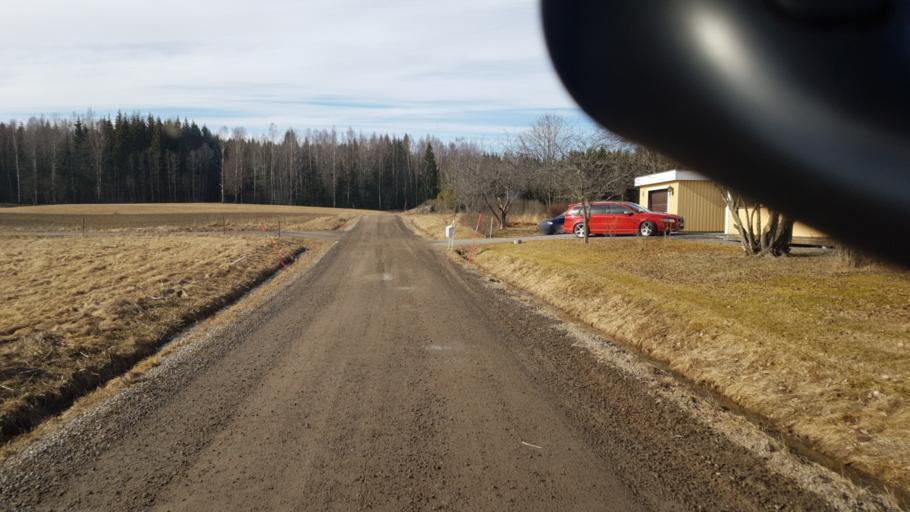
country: SE
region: Vaermland
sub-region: Eda Kommun
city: Amotfors
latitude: 59.8363
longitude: 12.3573
